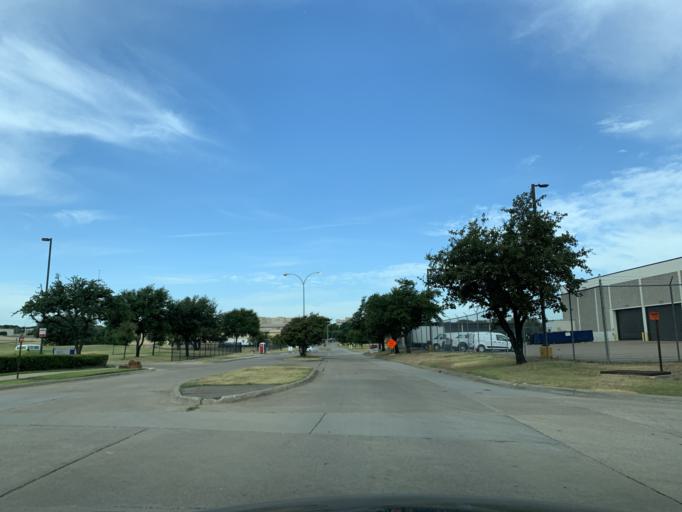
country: US
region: Texas
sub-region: Dallas County
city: Cockrell Hill
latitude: 32.7687
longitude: -96.8610
